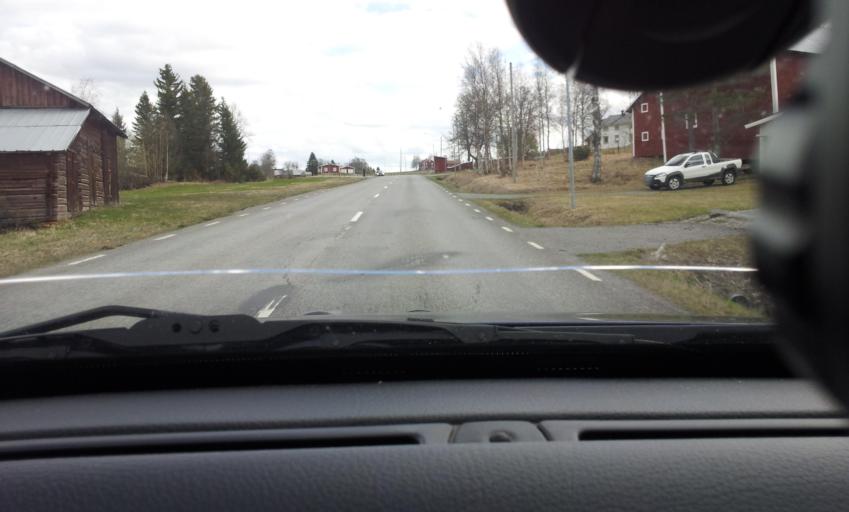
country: SE
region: Jaemtland
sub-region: OEstersunds Kommun
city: Ostersund
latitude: 63.1265
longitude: 14.6863
